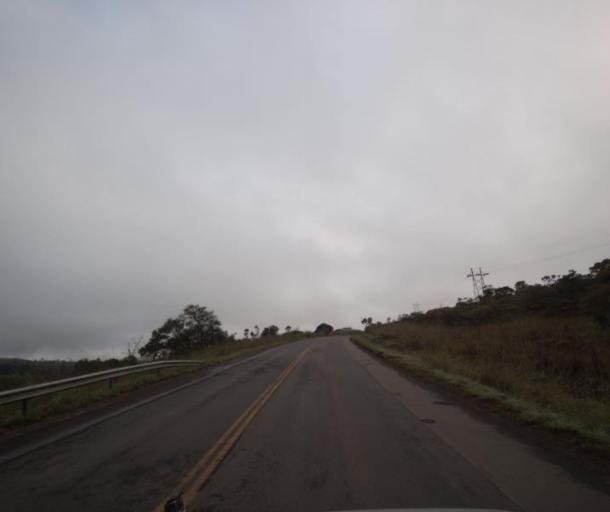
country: BR
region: Goias
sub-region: Pirenopolis
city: Pirenopolis
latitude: -15.8102
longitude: -48.7824
